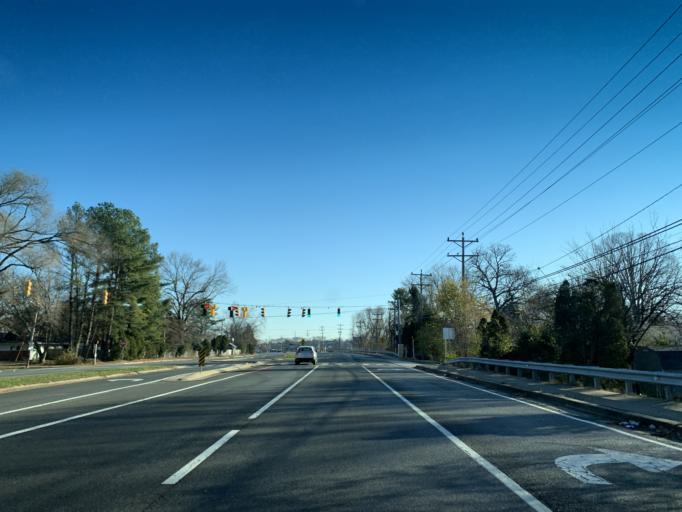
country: US
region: Delaware
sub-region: New Castle County
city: Brookside
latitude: 39.6619
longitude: -75.7310
